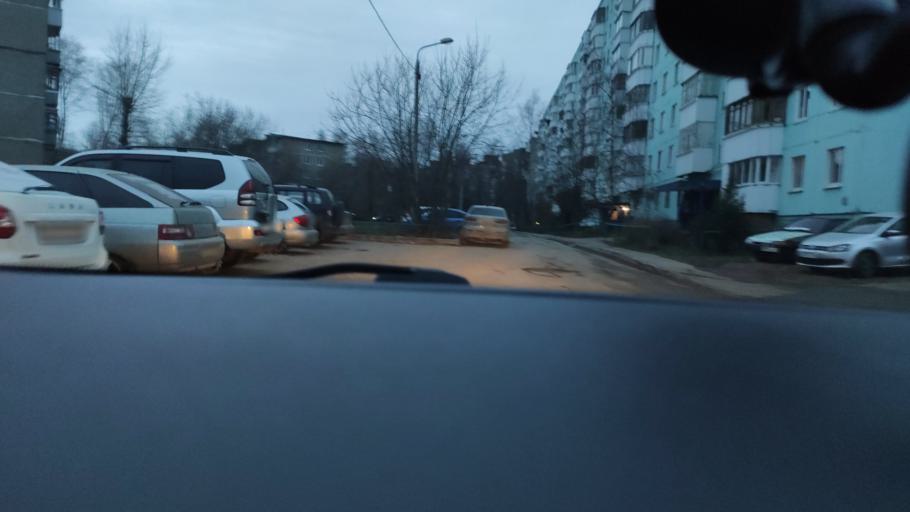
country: RU
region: Perm
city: Perm
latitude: 57.9678
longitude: 56.1918
